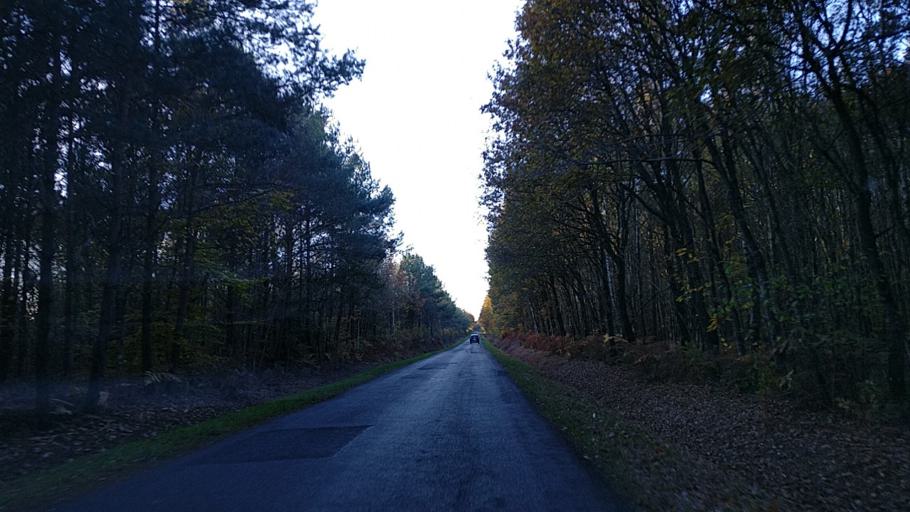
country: FR
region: Brittany
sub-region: Departement d'Ille-et-Vilaine
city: Saint-Sulpice-la-Foret
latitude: 48.1926
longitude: -1.5659
